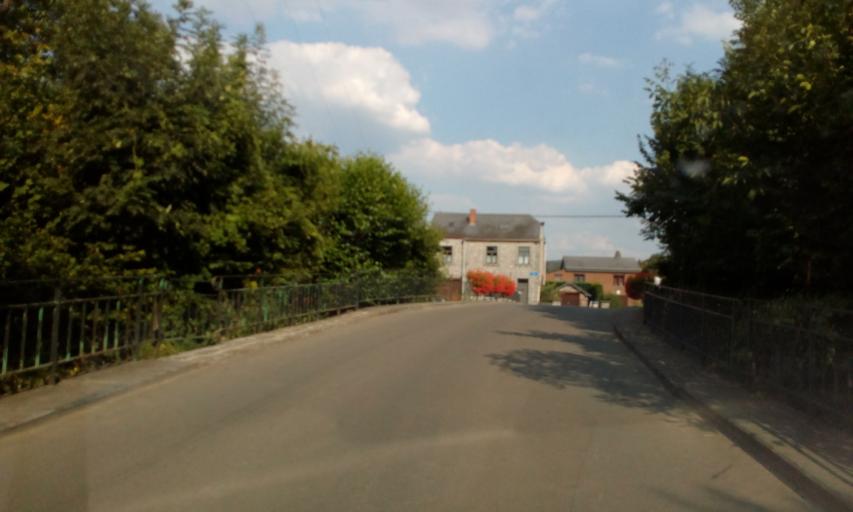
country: BE
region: Wallonia
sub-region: Province du Luxembourg
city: Tellin
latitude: 50.1070
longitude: 5.1961
